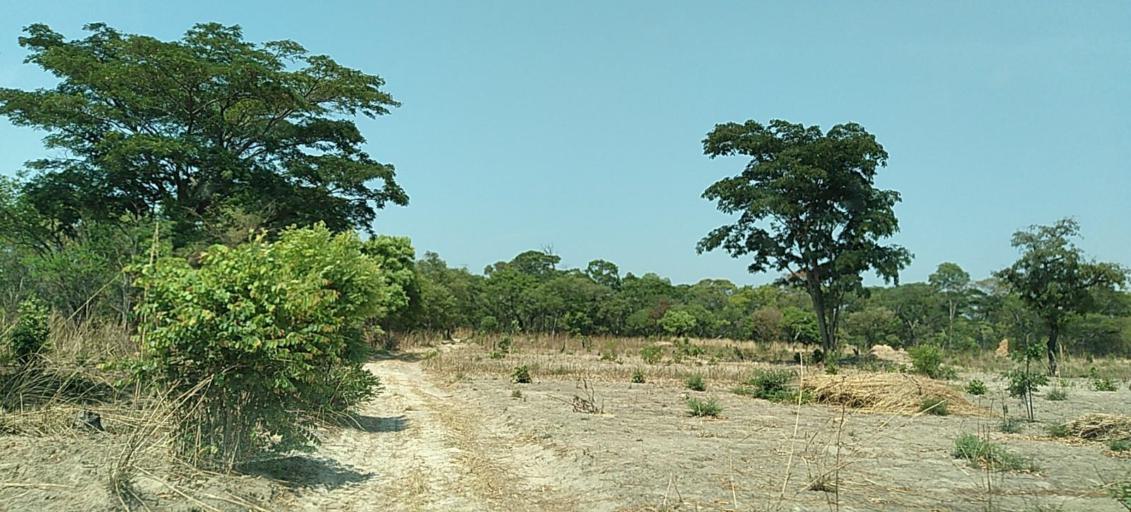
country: ZM
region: Copperbelt
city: Mpongwe
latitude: -13.7931
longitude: 28.0890
